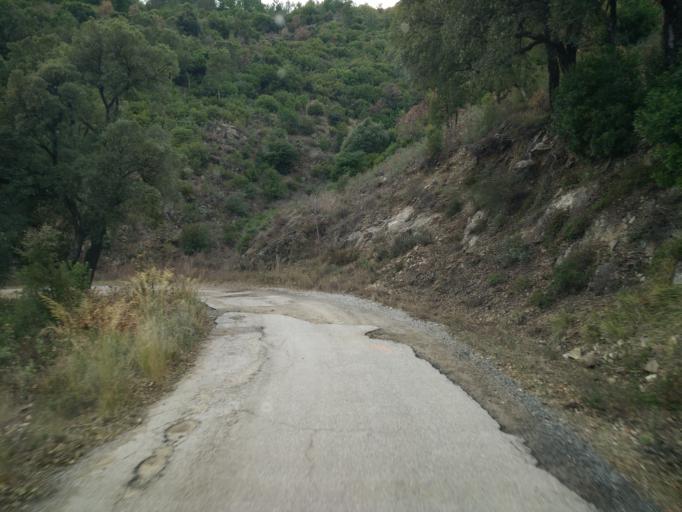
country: FR
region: Provence-Alpes-Cote d'Azur
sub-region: Departement du Var
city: Roquebrune-sur-Argens
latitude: 43.3899
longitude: 6.6104
